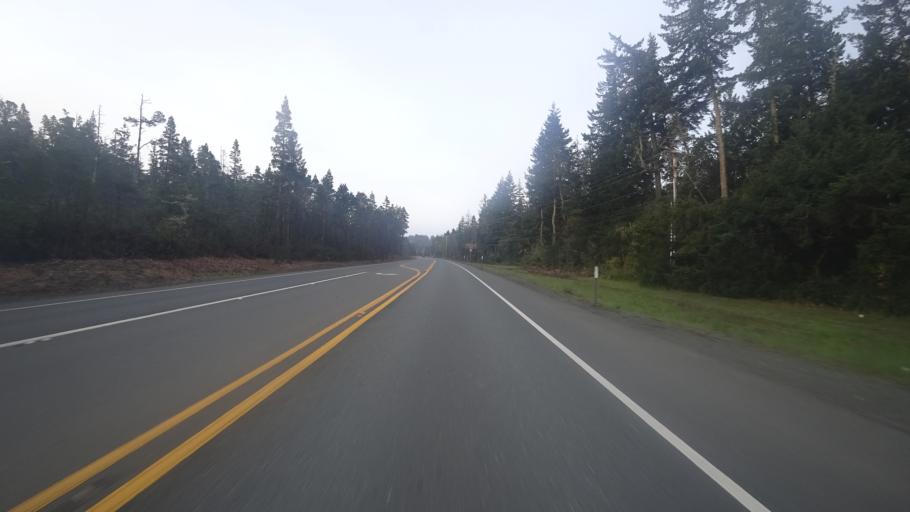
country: US
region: Oregon
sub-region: Coos County
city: Lakeside
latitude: 43.5870
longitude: -124.1842
